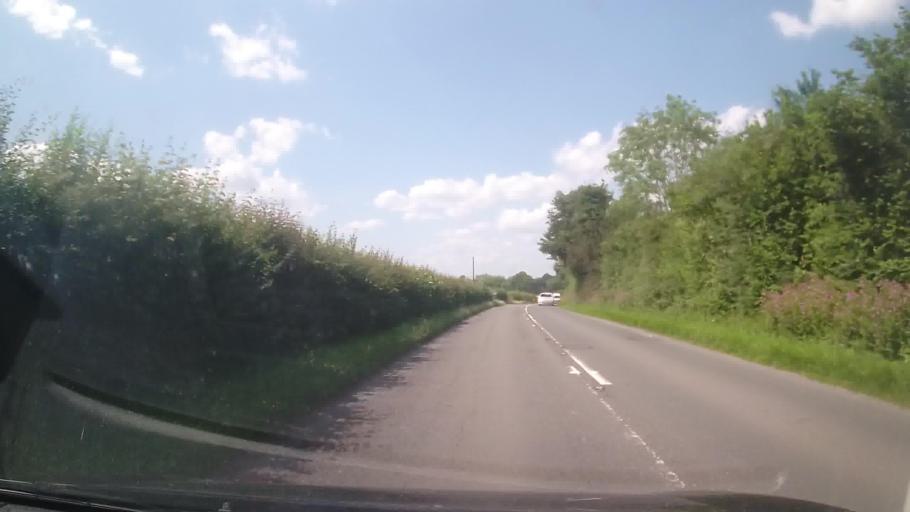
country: GB
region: England
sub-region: Herefordshire
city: Ocle Pychard
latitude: 52.1135
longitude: -2.5783
